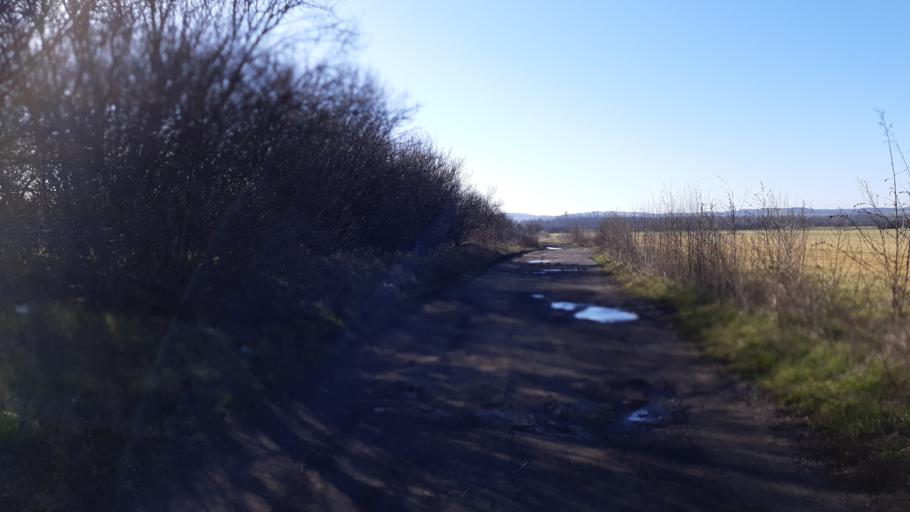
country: HU
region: Baranya
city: Pellerd
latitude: 46.0541
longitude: 18.1878
